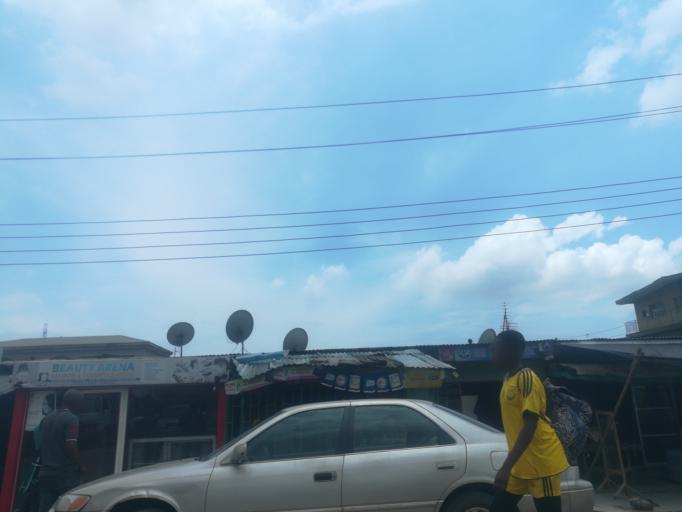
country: NG
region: Lagos
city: Somolu
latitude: 6.5529
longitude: 3.3924
